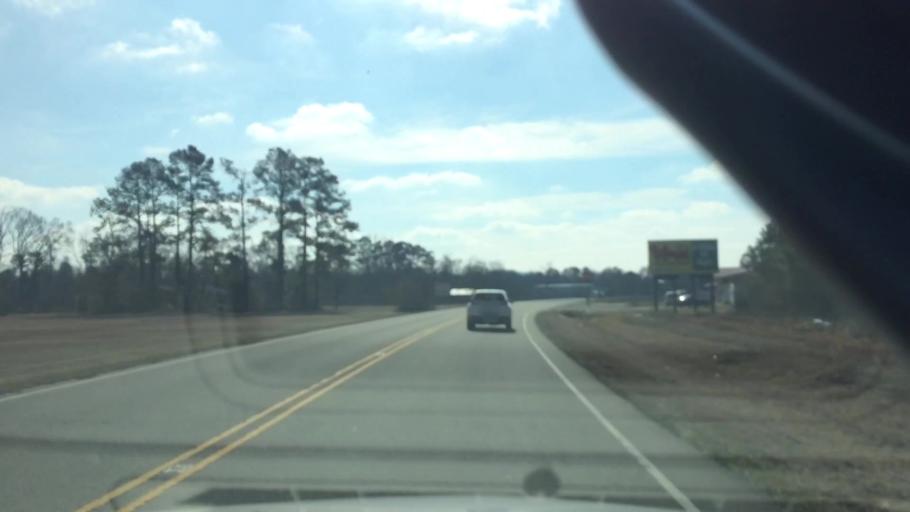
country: US
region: North Carolina
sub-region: Duplin County
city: Beulaville
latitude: 34.8224
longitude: -77.8394
